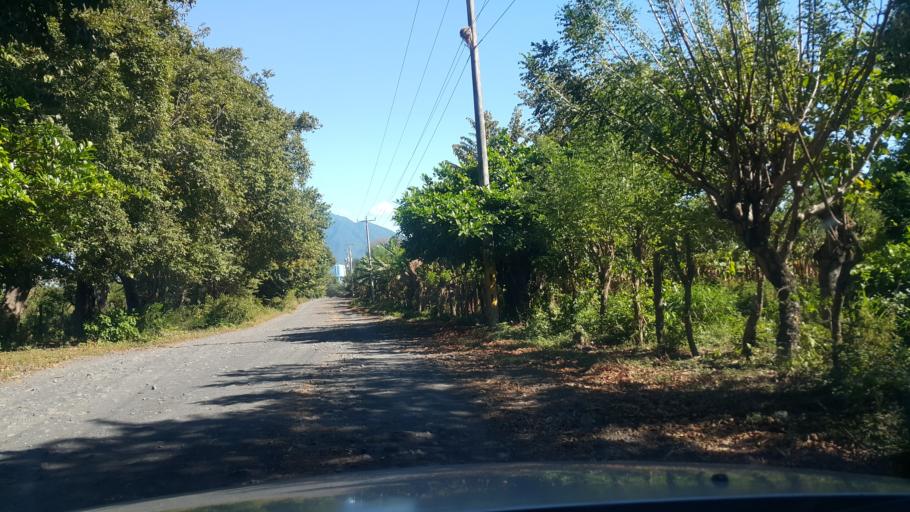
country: NI
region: Rivas
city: Altagracia
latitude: 11.4910
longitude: -85.6166
